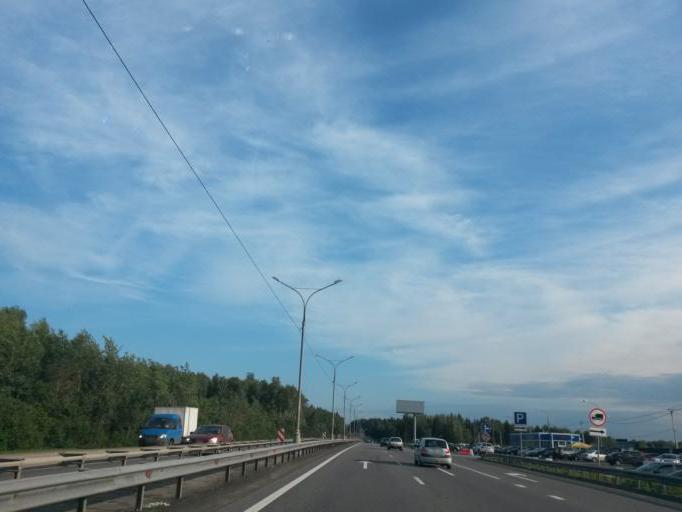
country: RU
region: Moskovskaya
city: Vostryakovo
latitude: 55.4668
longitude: 37.8537
